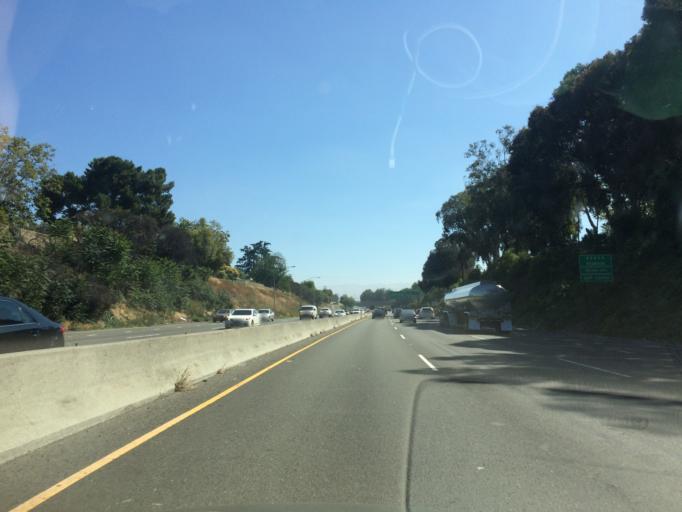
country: US
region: California
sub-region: Santa Clara County
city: Burbank
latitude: 37.3393
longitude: -121.9303
